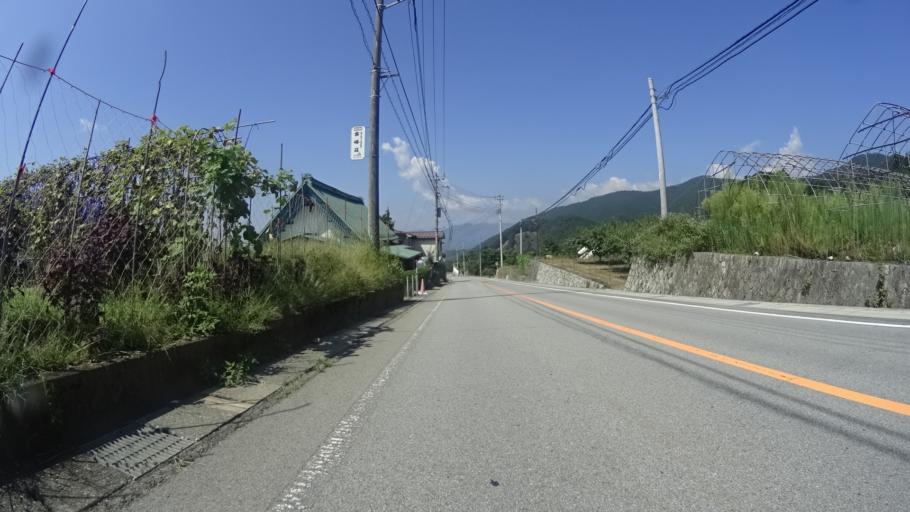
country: JP
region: Yamanashi
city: Enzan
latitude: 35.7314
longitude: 138.7787
